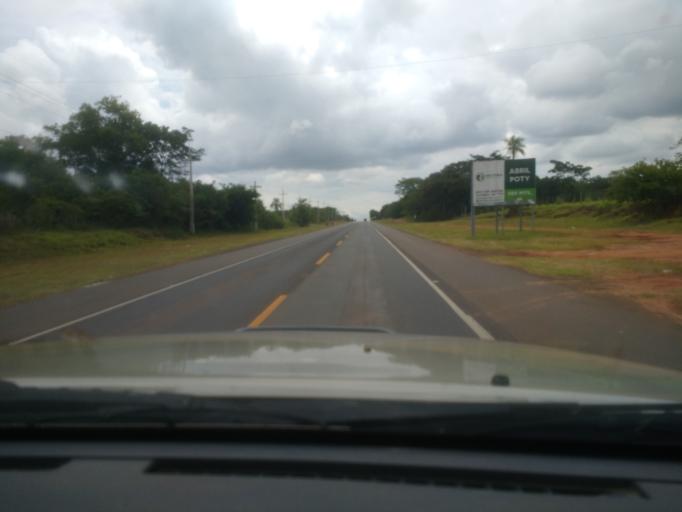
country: PY
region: Cordillera
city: Arroyos y Esteros
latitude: -25.0579
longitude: -57.1440
